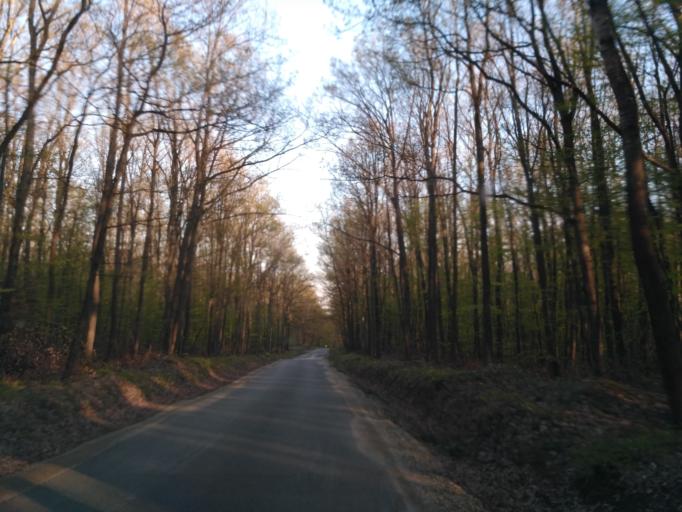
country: SK
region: Kosicky
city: Kosice
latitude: 48.7210
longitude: 21.1887
